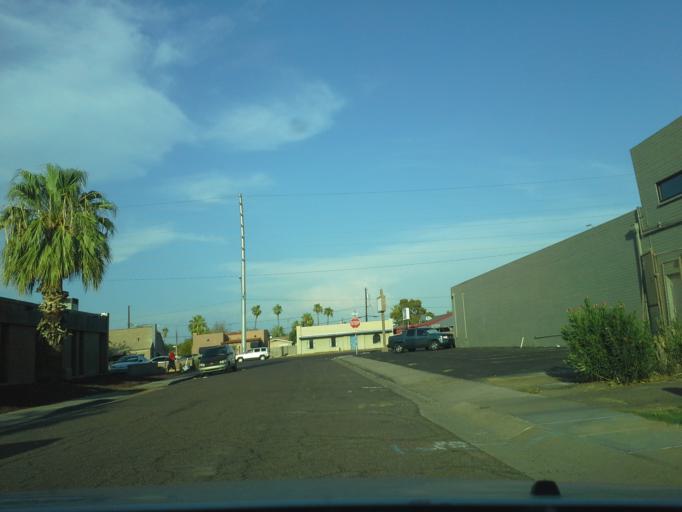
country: US
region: Arizona
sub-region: Maricopa County
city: Phoenix
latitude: 33.4725
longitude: -112.0660
